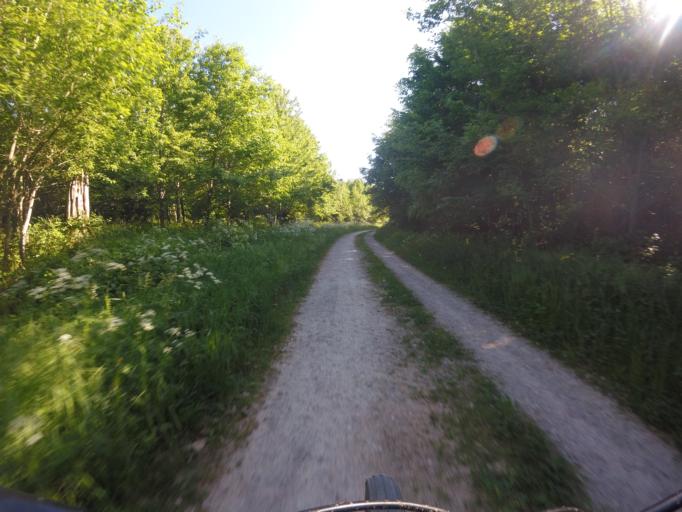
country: DE
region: Baden-Wuerttemberg
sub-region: Regierungsbezirk Stuttgart
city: Aspach
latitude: 48.9864
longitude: 9.4248
